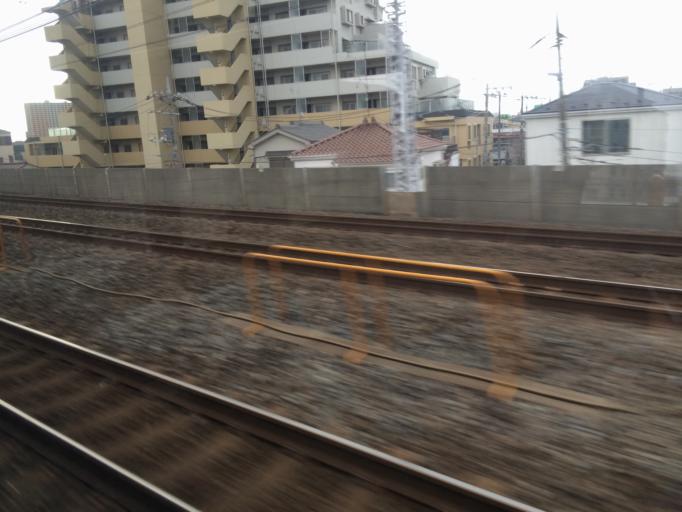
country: JP
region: Chiba
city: Matsudo
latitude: 35.7360
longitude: 139.8903
